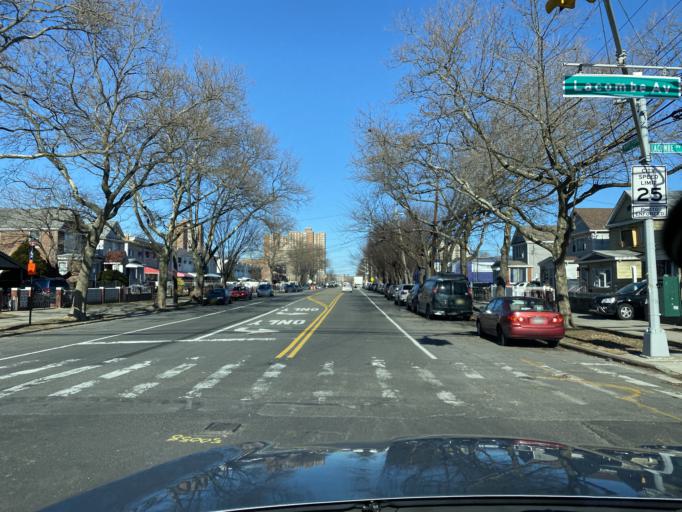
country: US
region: New York
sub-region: Bronx
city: The Bronx
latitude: 40.8157
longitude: -73.8568
